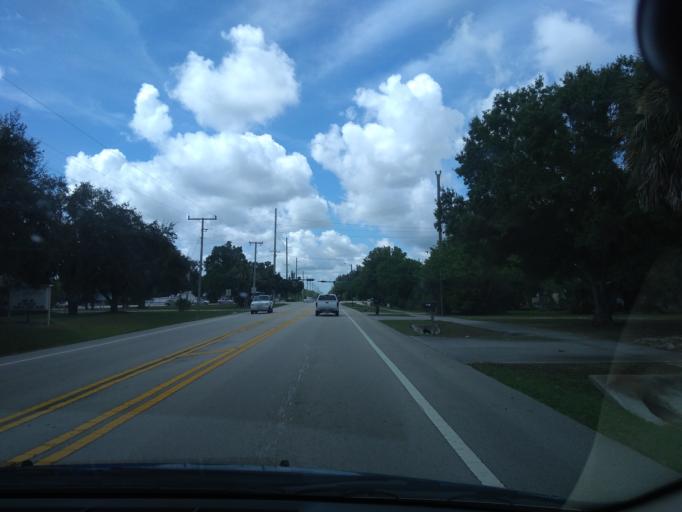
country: US
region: Florida
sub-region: Indian River County
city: Vero Beach South
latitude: 27.6252
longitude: -80.4139
